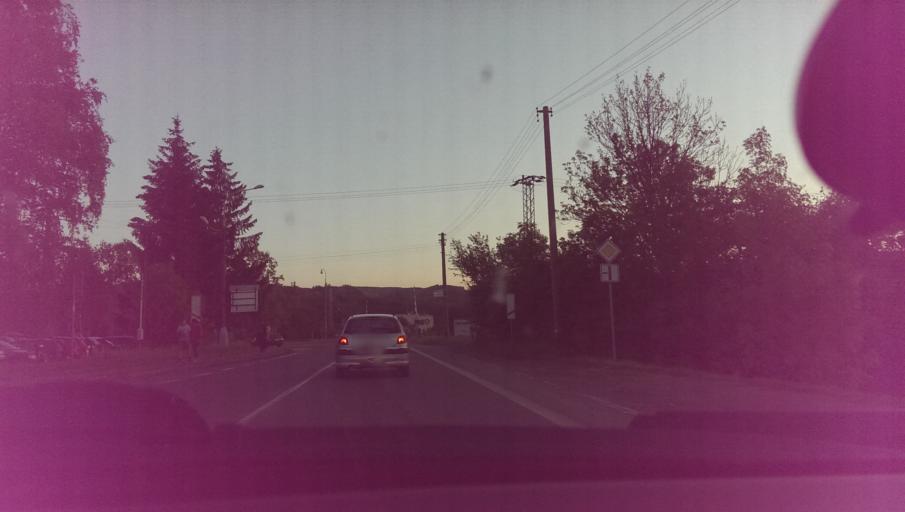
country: CZ
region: Zlin
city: Jablunka
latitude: 49.3800
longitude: 17.9480
